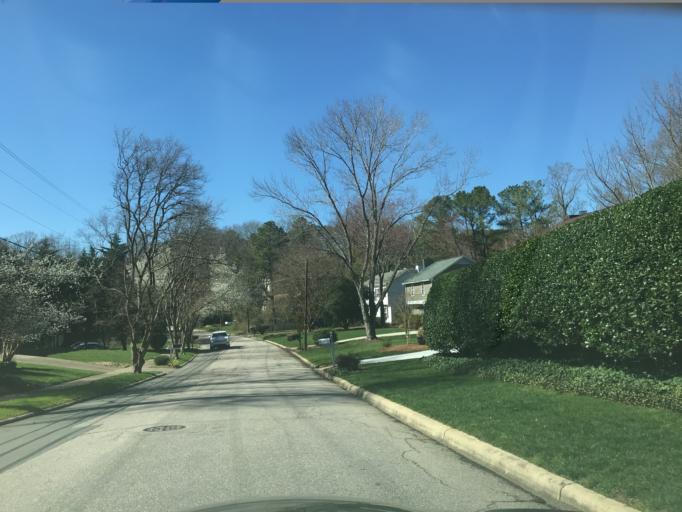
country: US
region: North Carolina
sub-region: Wake County
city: West Raleigh
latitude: 35.8489
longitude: -78.6229
